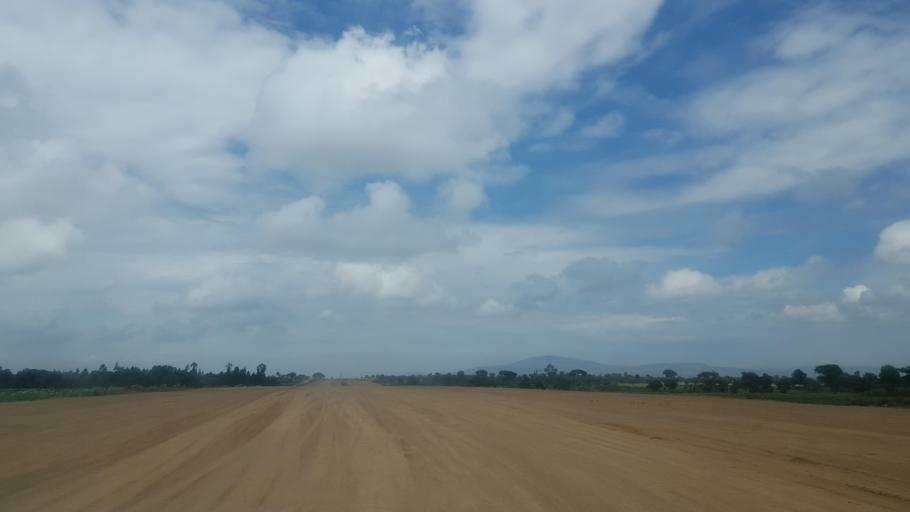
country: ET
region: Oromiya
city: Shashemene
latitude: 7.2435
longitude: 38.5840
